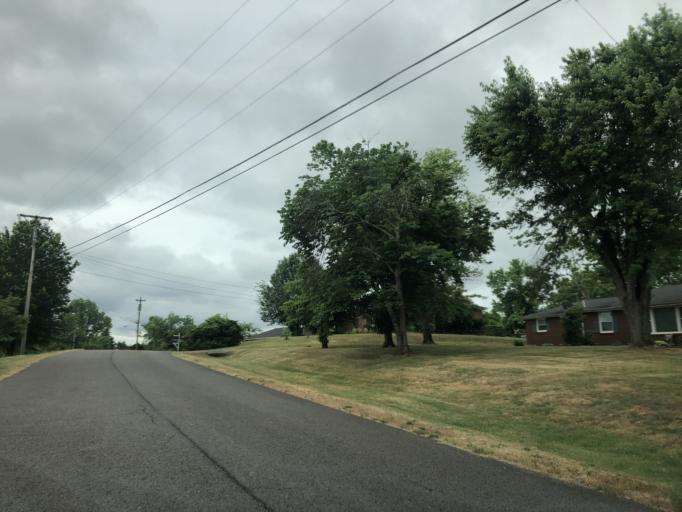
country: US
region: Tennessee
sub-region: Davidson County
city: Goodlettsville
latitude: 36.2646
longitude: -86.7698
